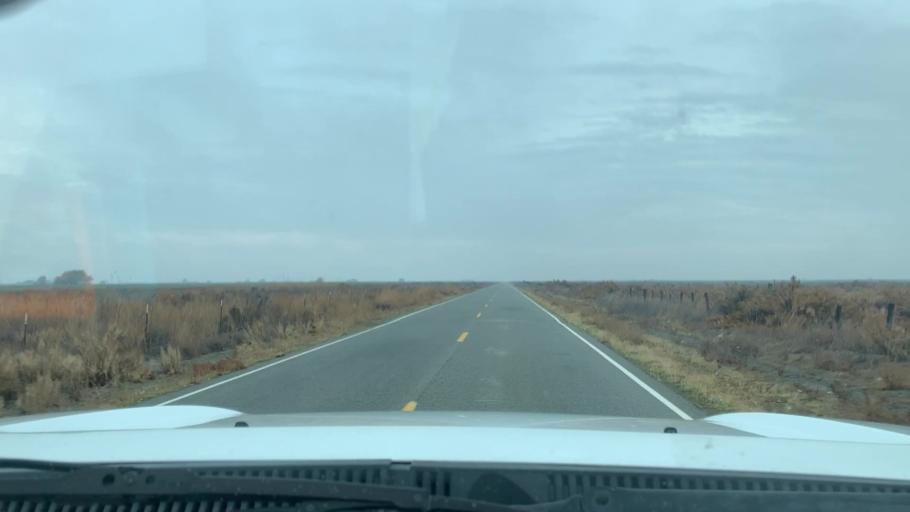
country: US
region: California
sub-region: Kern County
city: Lost Hills
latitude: 35.7341
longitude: -119.5794
